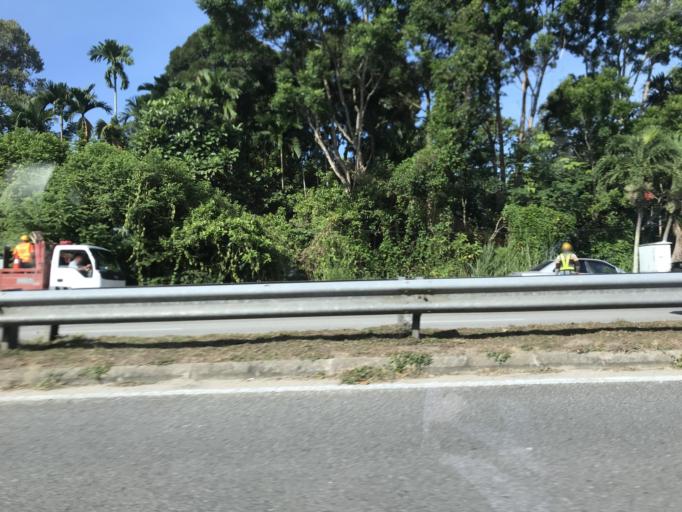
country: MY
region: Kelantan
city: Pasir Mas
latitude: 6.0615
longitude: 102.2082
